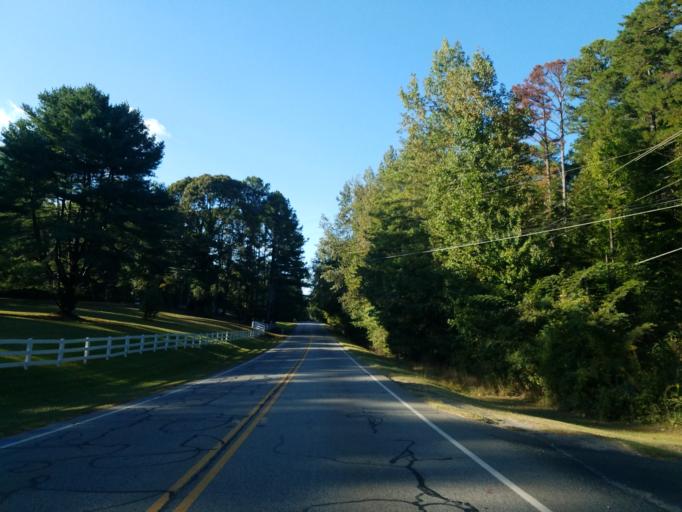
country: US
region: Georgia
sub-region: Bartow County
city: Cartersville
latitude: 34.0920
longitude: -84.8436
